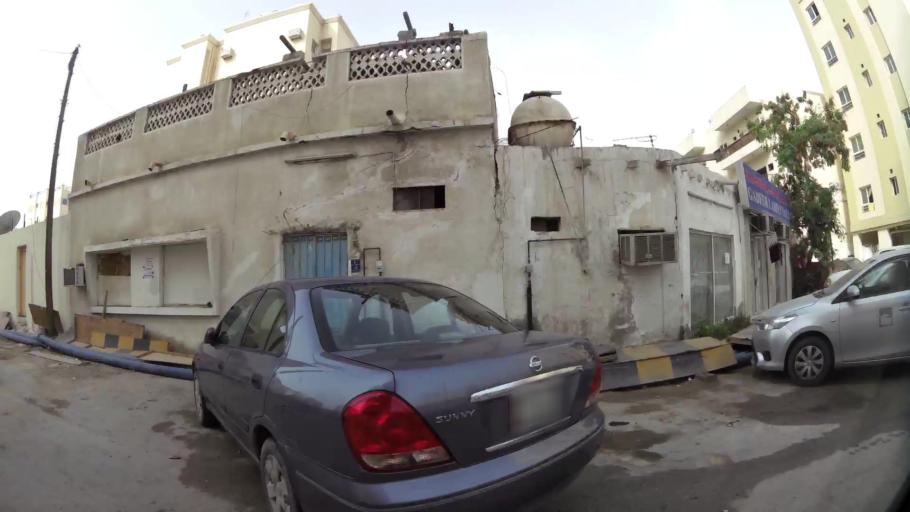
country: QA
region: Baladiyat ad Dawhah
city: Doha
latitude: 25.2815
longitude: 51.5470
